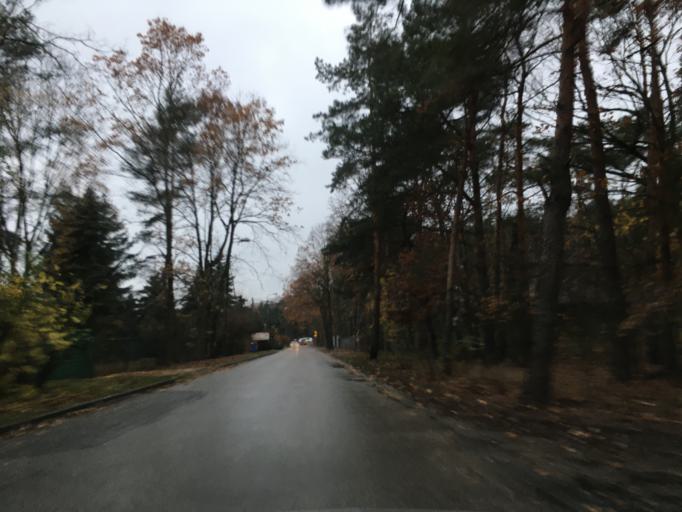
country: PL
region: Masovian Voivodeship
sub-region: Powiat piaseczynski
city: Lesznowola
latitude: 52.0925
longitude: 20.8854
